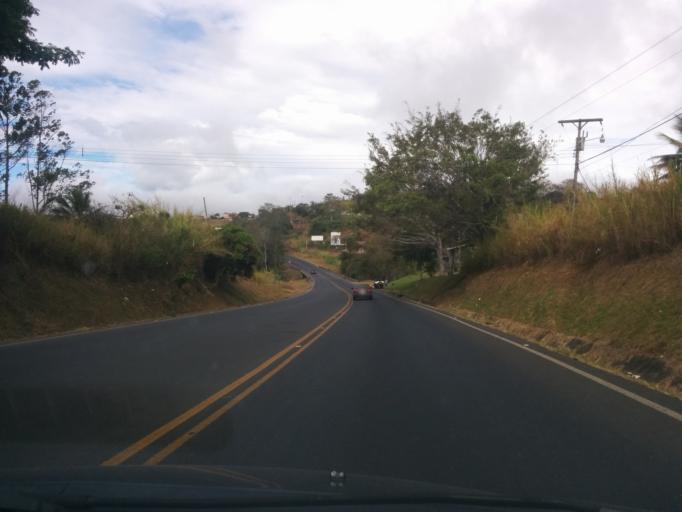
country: CR
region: Alajuela
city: San Ramon
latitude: 10.0793
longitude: -84.4590
